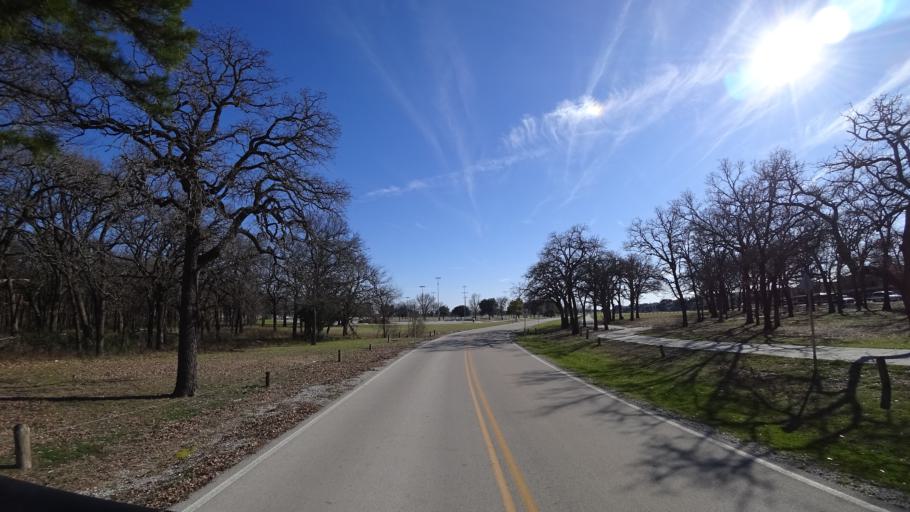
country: US
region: Texas
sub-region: Denton County
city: Lewisville
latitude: 33.0758
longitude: -97.0071
